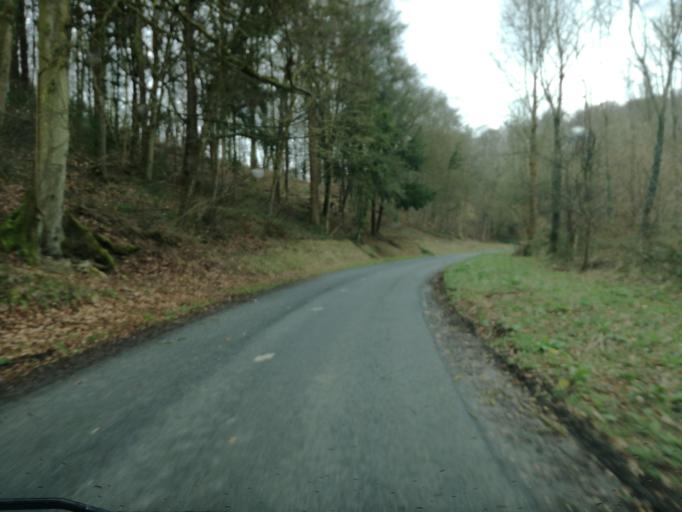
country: FR
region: Haute-Normandie
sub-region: Departement de la Seine-Maritime
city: Caudebec-en-Caux
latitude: 49.5600
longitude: 0.7408
